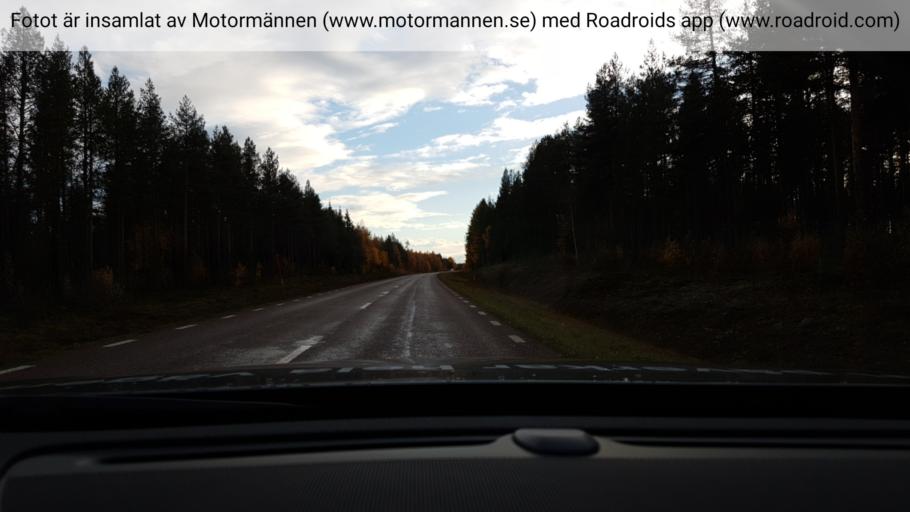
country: SE
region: Norrbotten
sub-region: Pajala Kommun
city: Pajala
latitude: 67.1483
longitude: 22.6248
